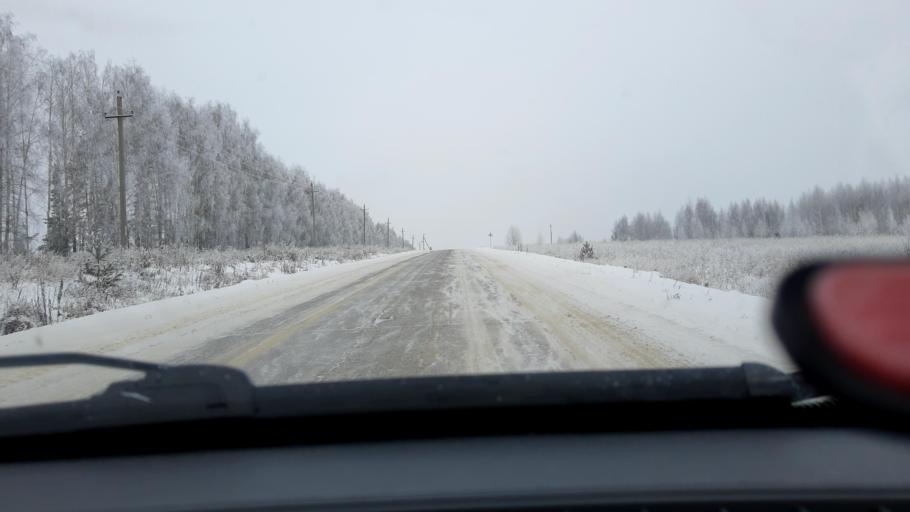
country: RU
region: Bashkortostan
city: Iglino
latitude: 54.6550
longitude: 56.4257
